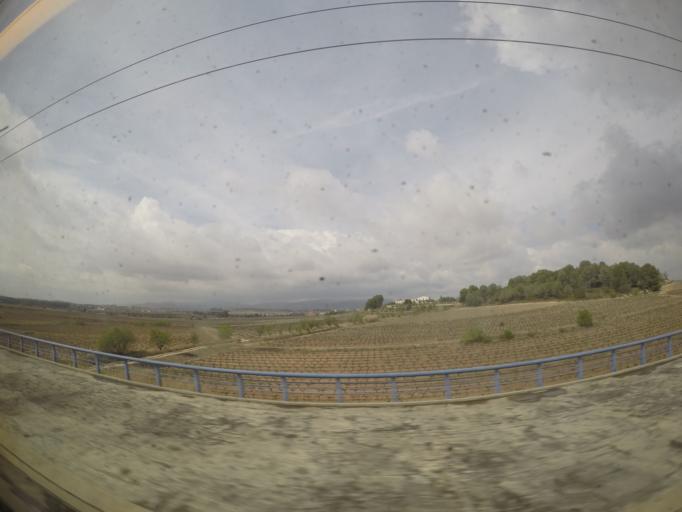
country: ES
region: Catalonia
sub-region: Provincia de Barcelona
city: Castellet
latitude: 41.2701
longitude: 1.5959
